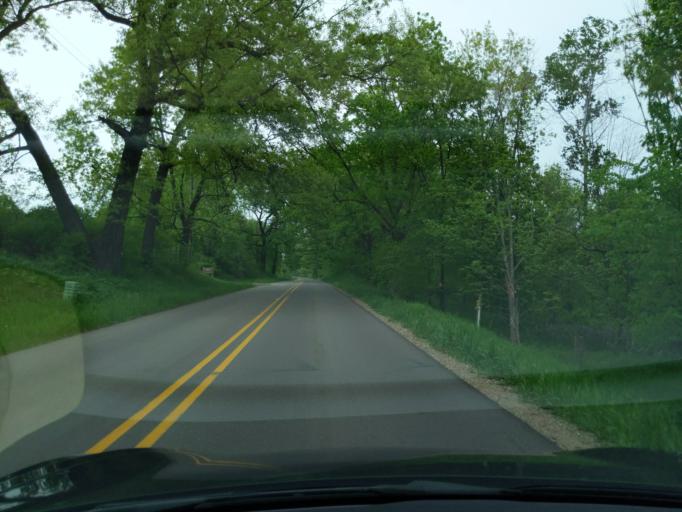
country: US
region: Michigan
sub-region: Ingham County
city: Leslie
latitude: 42.4224
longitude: -84.3561
